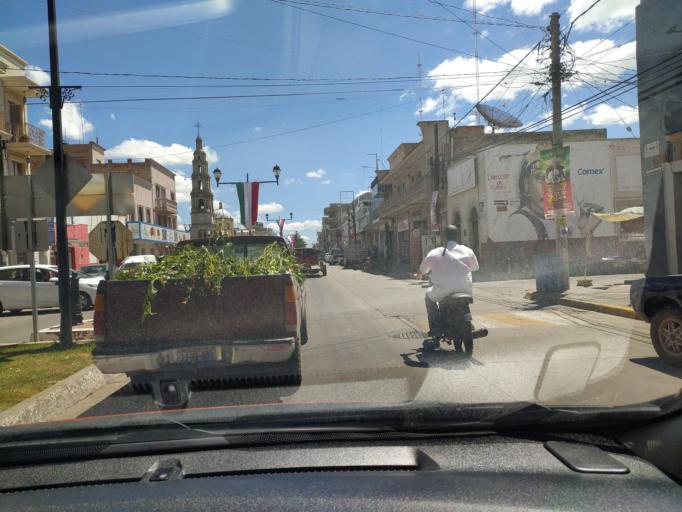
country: MX
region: Jalisco
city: San Julian
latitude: 21.0110
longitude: -102.1815
